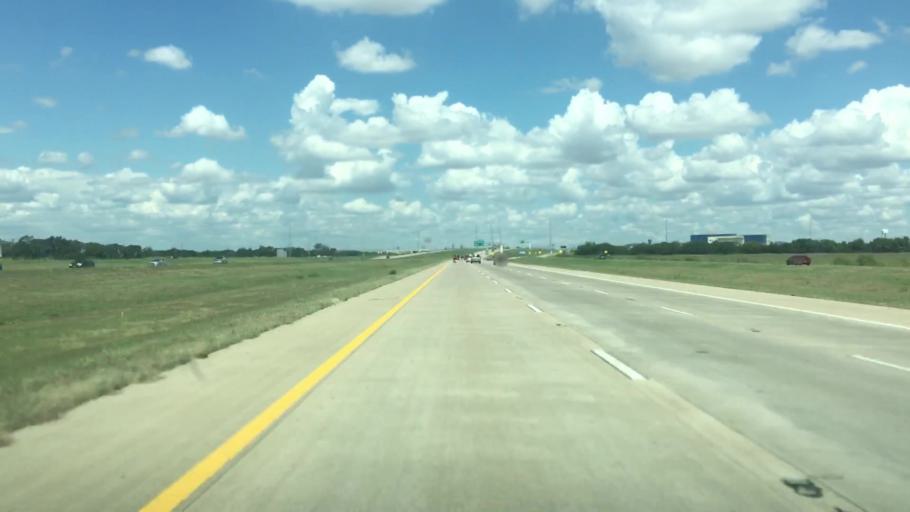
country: US
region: Texas
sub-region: Travis County
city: Pflugerville
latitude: 30.4408
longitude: -97.5922
